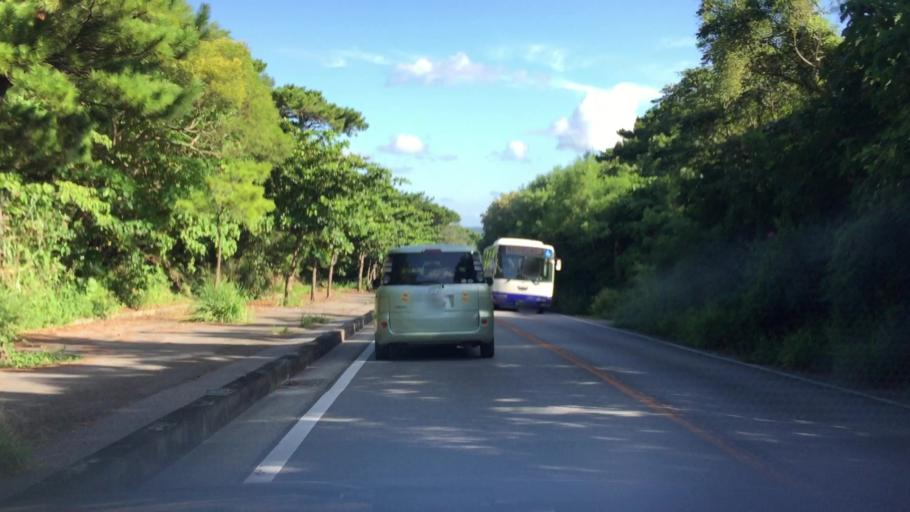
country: JP
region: Okinawa
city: Ishigaki
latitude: 24.4376
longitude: 124.1194
